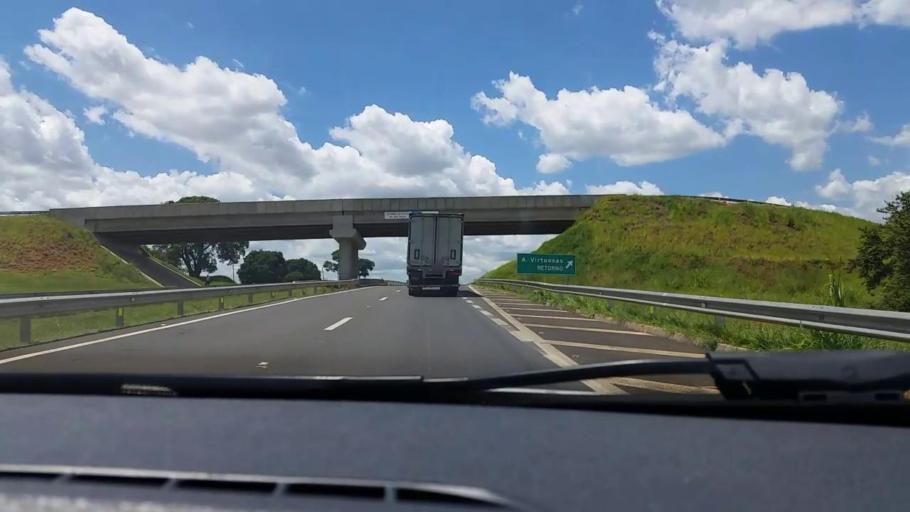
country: BR
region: Sao Paulo
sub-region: Bauru
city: Bauru
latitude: -22.3992
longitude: -49.0886
